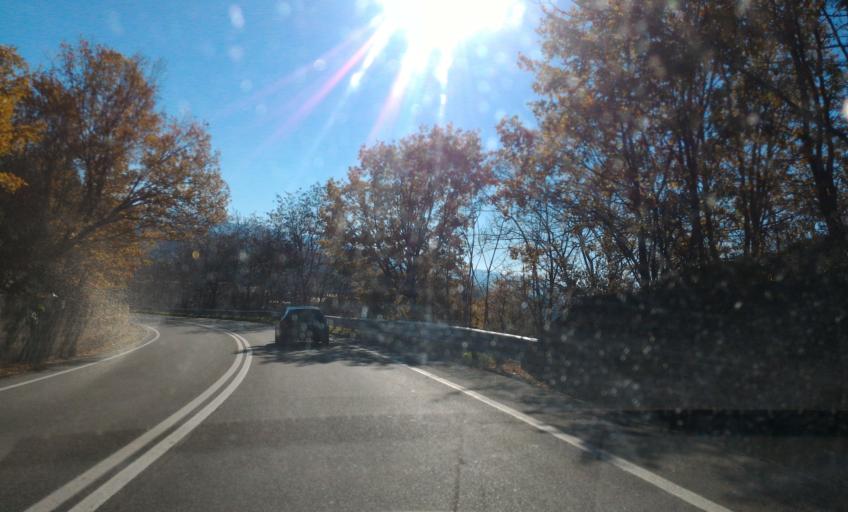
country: IT
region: Calabria
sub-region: Provincia di Cosenza
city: Rovito
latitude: 39.3046
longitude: 16.3094
